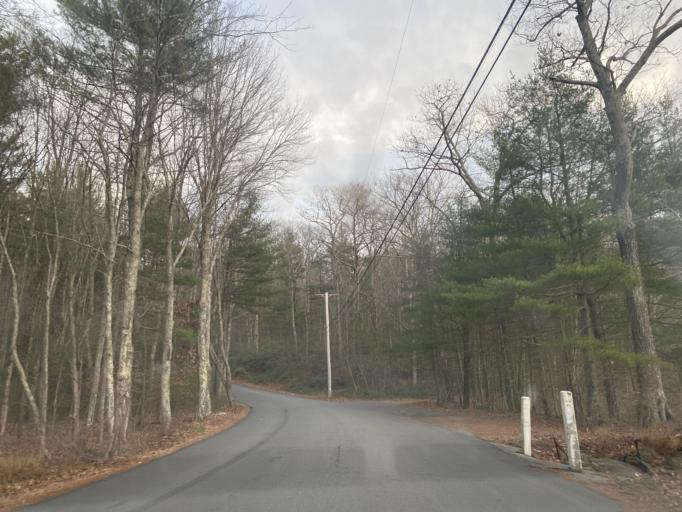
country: US
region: Massachusetts
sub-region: Worcester County
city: Leicester
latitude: 42.2641
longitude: -71.9491
